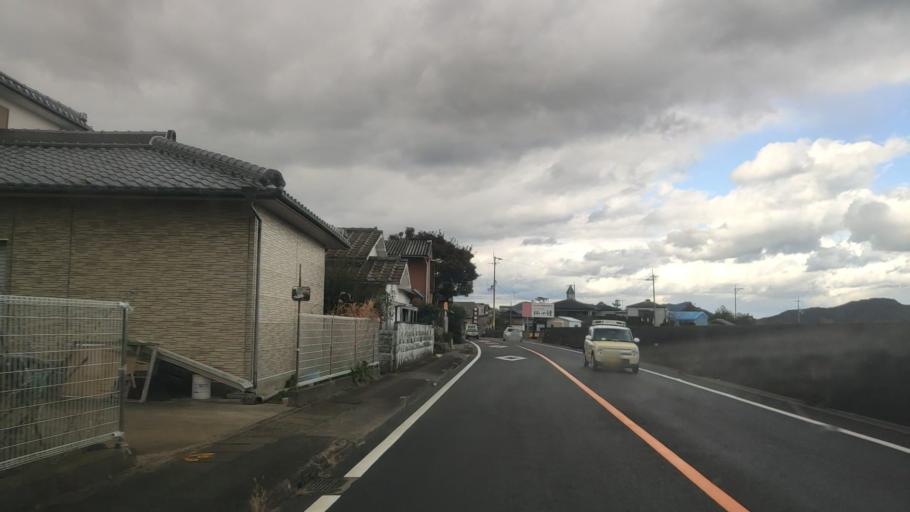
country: JP
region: Tokushima
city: Ishii
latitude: 34.2186
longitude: 134.4160
